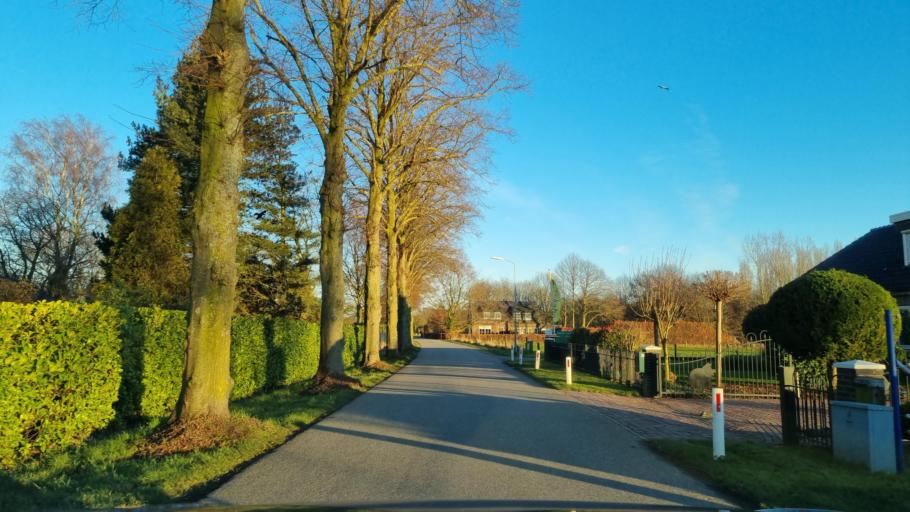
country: NL
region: Gelderland
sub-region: Gemeente Groesbeek
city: De Horst
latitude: 51.7745
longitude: 5.9738
